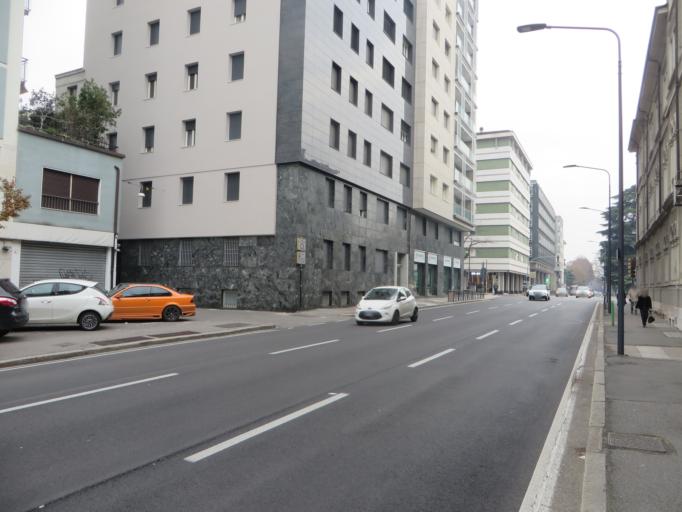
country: IT
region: Lombardy
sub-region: Provincia di Brescia
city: Brescia
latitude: 45.5343
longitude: 10.2172
